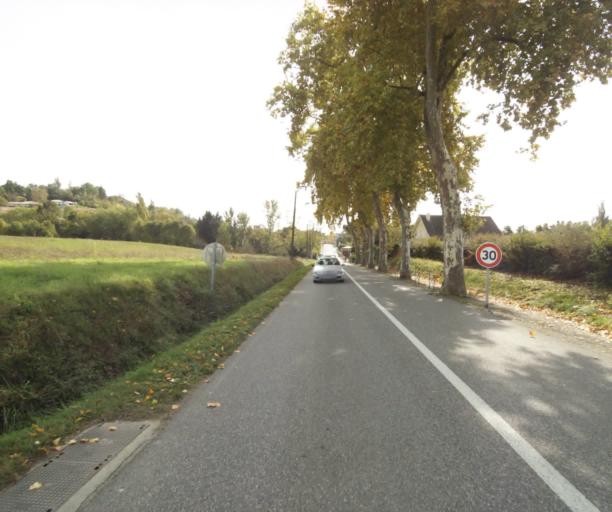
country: FR
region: Midi-Pyrenees
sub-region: Departement du Tarn-et-Garonne
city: Corbarieu
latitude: 43.9470
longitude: 1.3659
